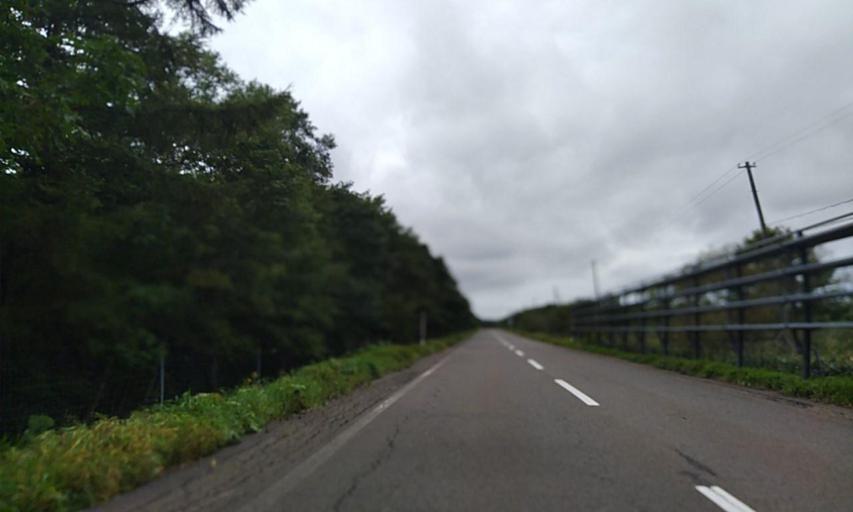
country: JP
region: Hokkaido
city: Nemuro
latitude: 43.3651
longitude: 145.2775
